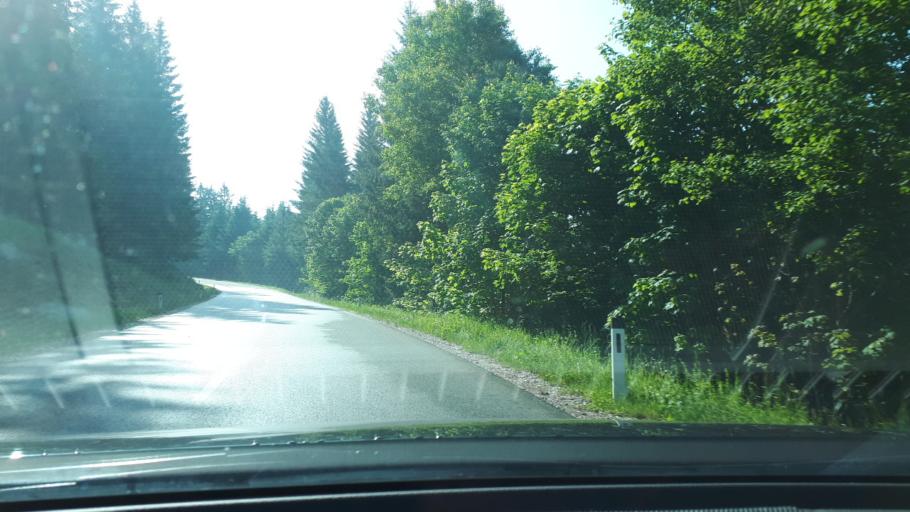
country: AT
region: Styria
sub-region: Politischer Bezirk Voitsberg
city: Pack
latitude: 46.9297
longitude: 14.9954
